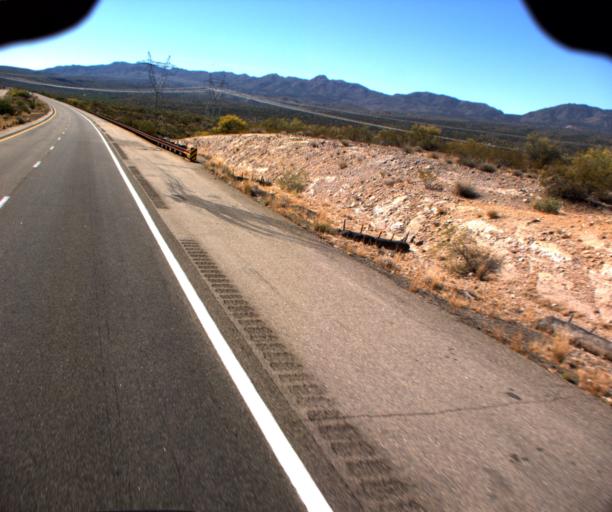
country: US
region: Arizona
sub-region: Yavapai County
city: Bagdad
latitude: 34.5330
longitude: -113.4321
